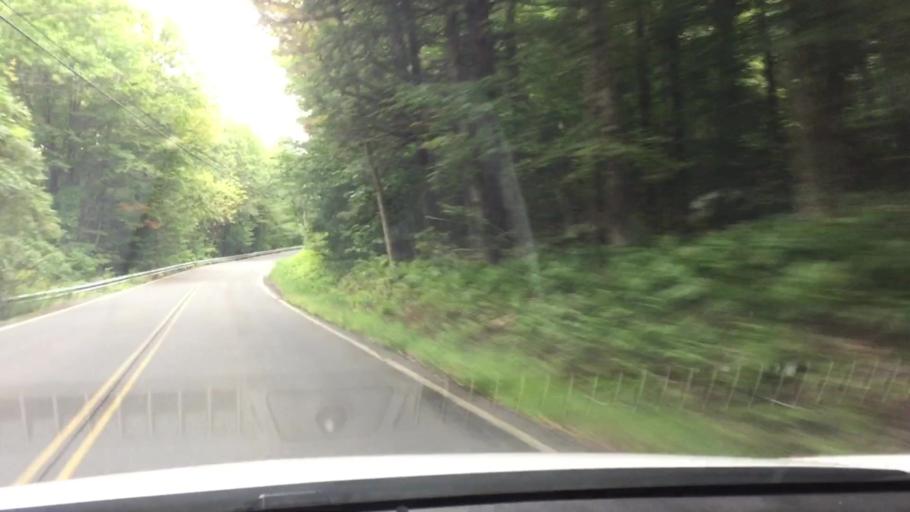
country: US
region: Massachusetts
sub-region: Berkshire County
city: Otis
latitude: 42.2216
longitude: -72.9587
